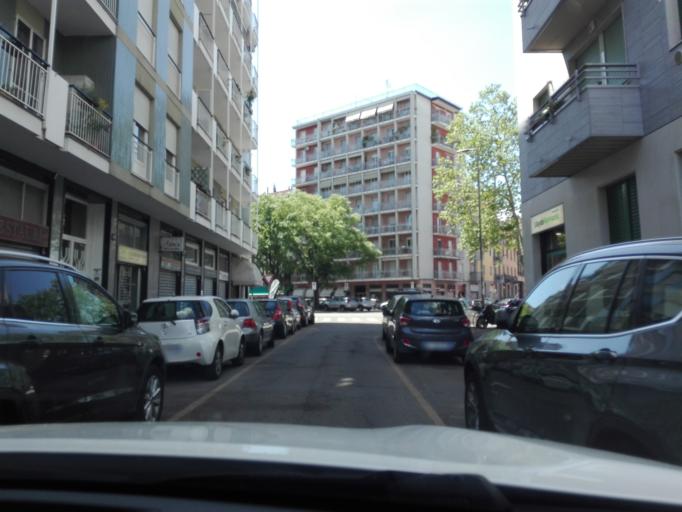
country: IT
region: Lombardy
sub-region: Citta metropolitana di Milano
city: Milano
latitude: 45.4605
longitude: 9.1575
